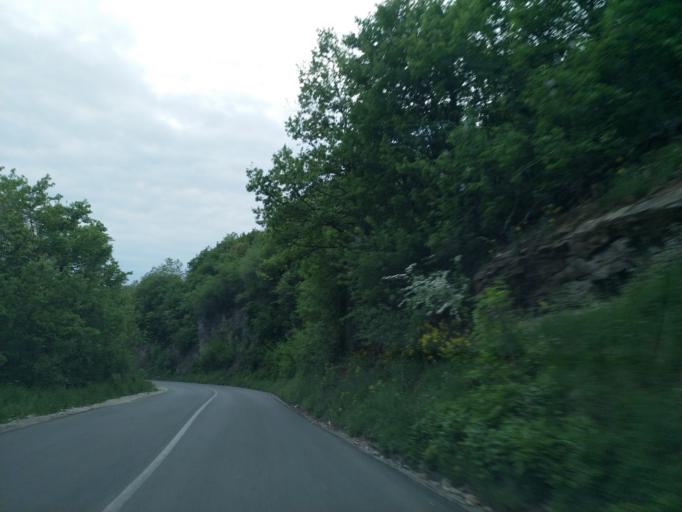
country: RS
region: Central Serbia
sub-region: Pomoravski Okrug
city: Despotovac
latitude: 43.9759
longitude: 21.5061
